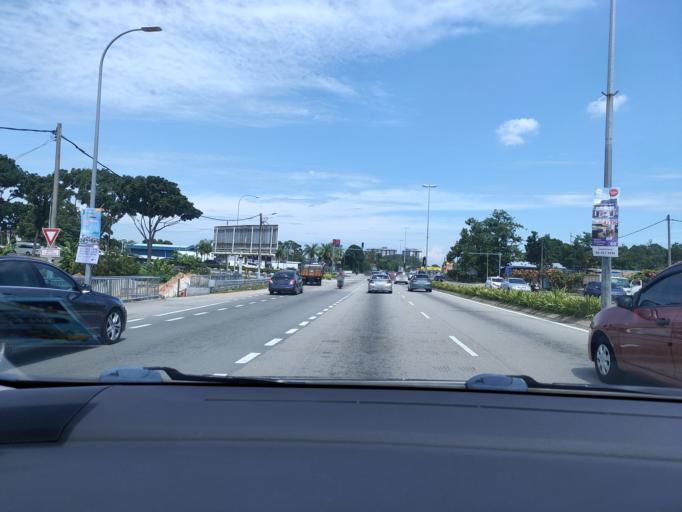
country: MY
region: Melaka
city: Batu Berendam
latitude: 2.2563
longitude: 102.2224
